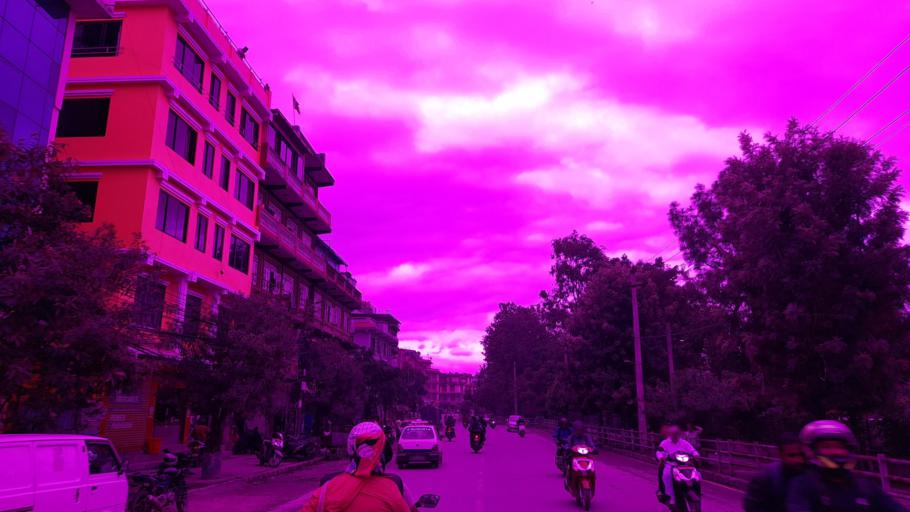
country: NP
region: Central Region
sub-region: Bagmati Zone
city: Kathmandu
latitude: 27.7114
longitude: 85.3028
